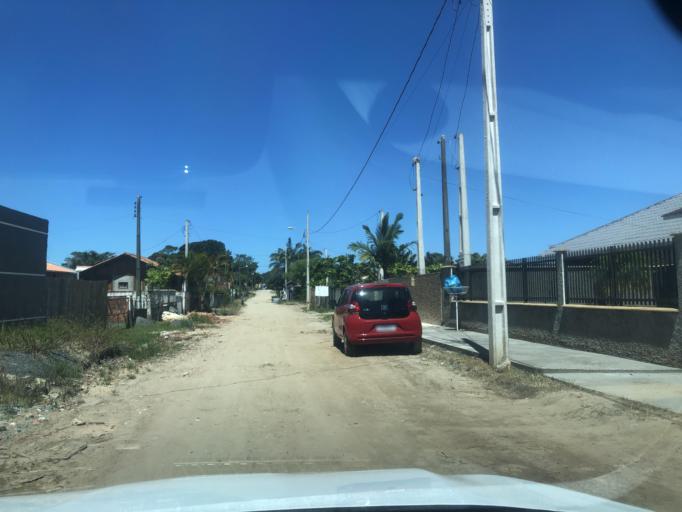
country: BR
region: Santa Catarina
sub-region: Sao Francisco Do Sul
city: Sao Francisco do Sul
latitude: -26.2260
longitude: -48.5228
